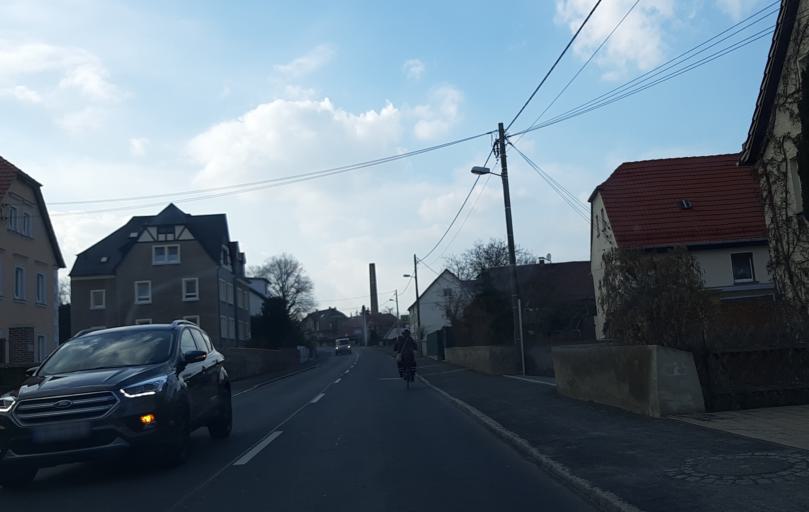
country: DE
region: Saxony
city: Grossenhain
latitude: 51.2881
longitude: 13.5034
